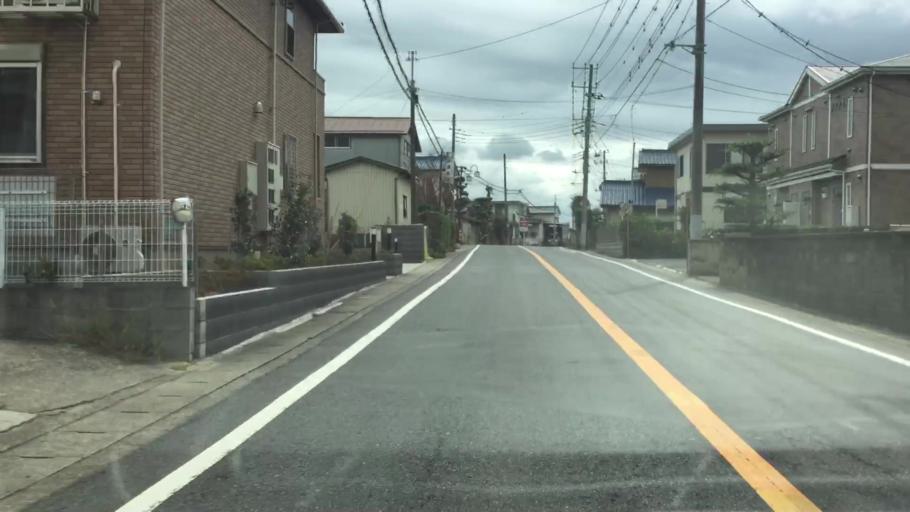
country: JP
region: Ibaraki
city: Ryugasaki
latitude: 35.8472
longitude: 140.1416
